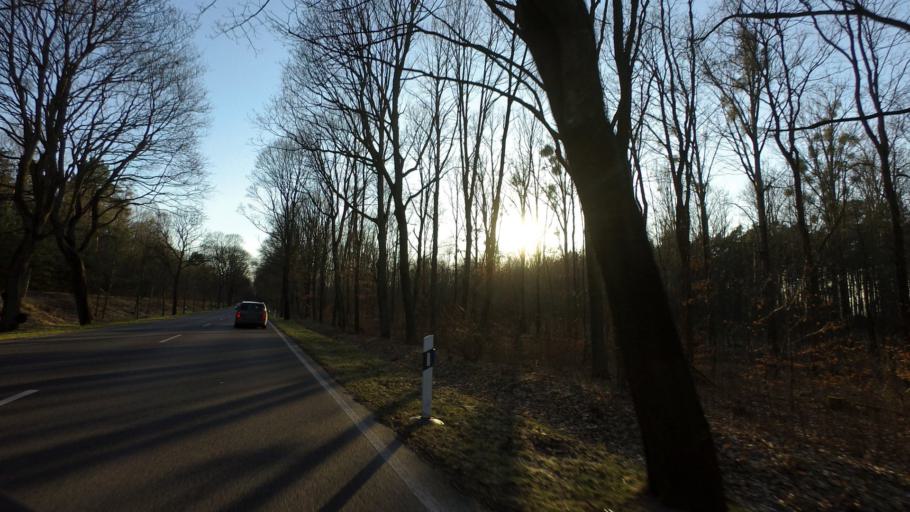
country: DE
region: Brandenburg
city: Werftpfuhl
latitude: 52.6726
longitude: 13.8208
